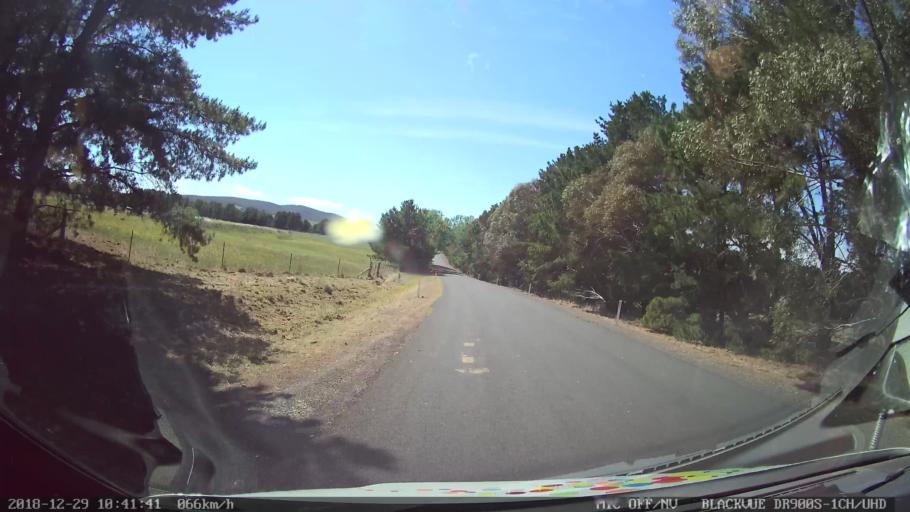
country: AU
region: New South Wales
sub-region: Palerang
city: Bungendore
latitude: -35.0277
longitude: 149.5223
